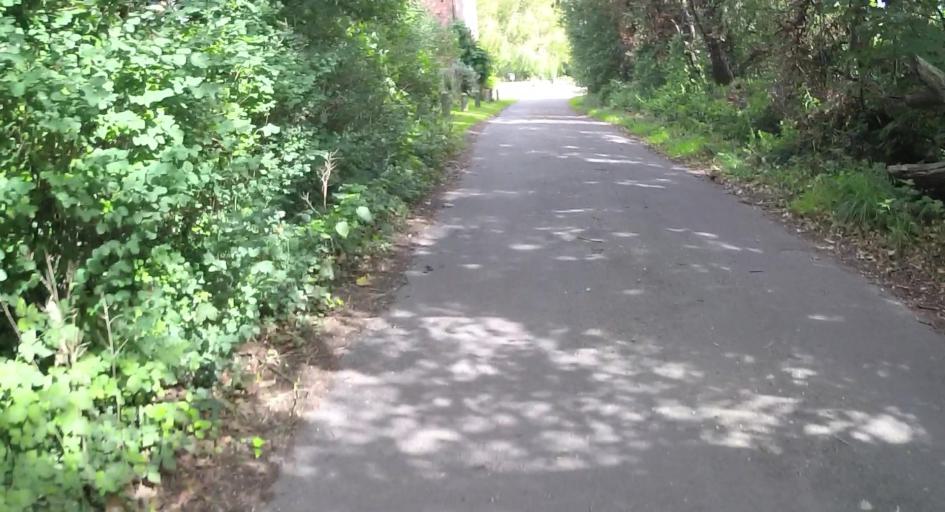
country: GB
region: England
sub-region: West Berkshire
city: Thatcham
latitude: 51.3915
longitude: -1.2408
